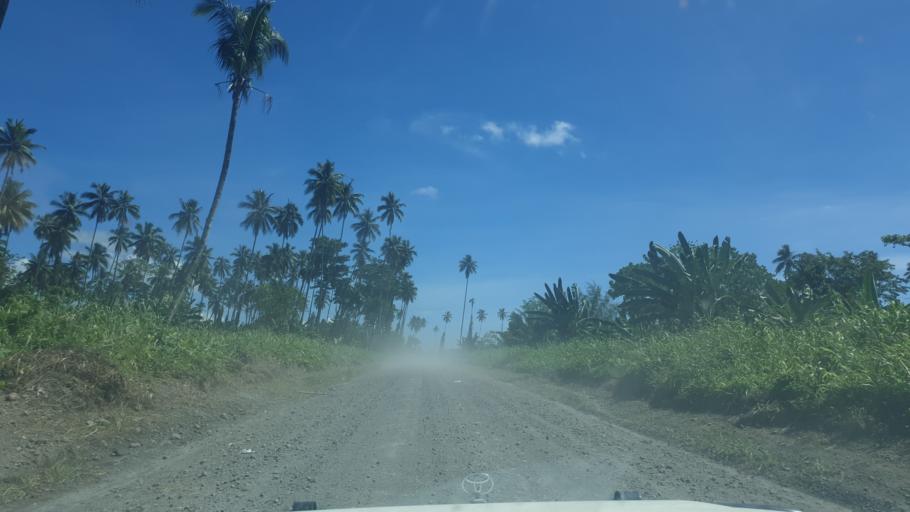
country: PG
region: Bougainville
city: Arawa
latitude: -5.9766
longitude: 155.3498
